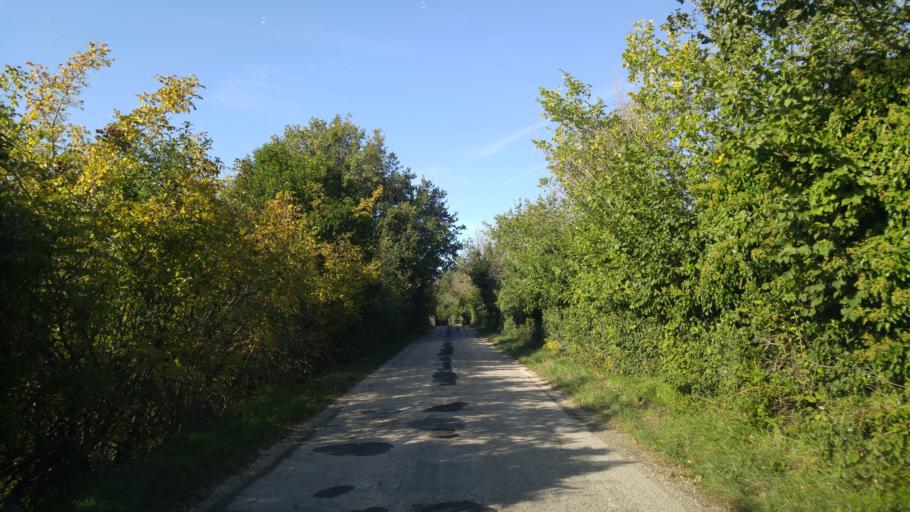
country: IT
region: The Marches
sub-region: Provincia di Pesaro e Urbino
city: Bellocchi
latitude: 43.7999
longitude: 13.0212
